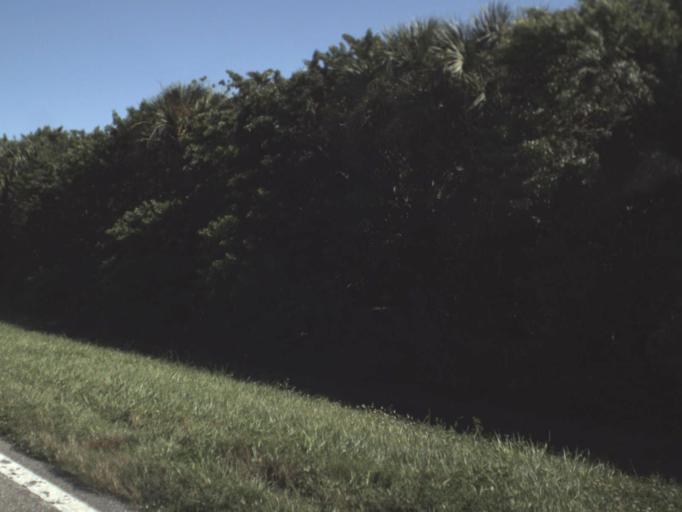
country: US
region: Florida
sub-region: Hendry County
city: Port LaBelle
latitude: 26.7685
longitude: -81.2932
